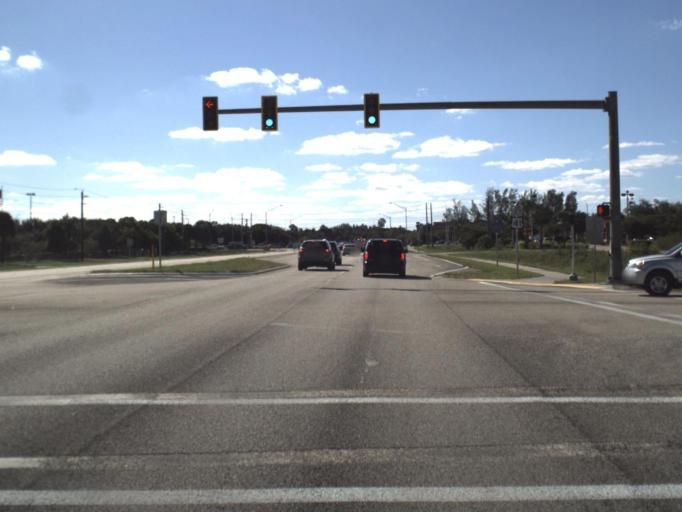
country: US
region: Florida
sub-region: Lee County
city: Villas
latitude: 26.5281
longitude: -81.8678
